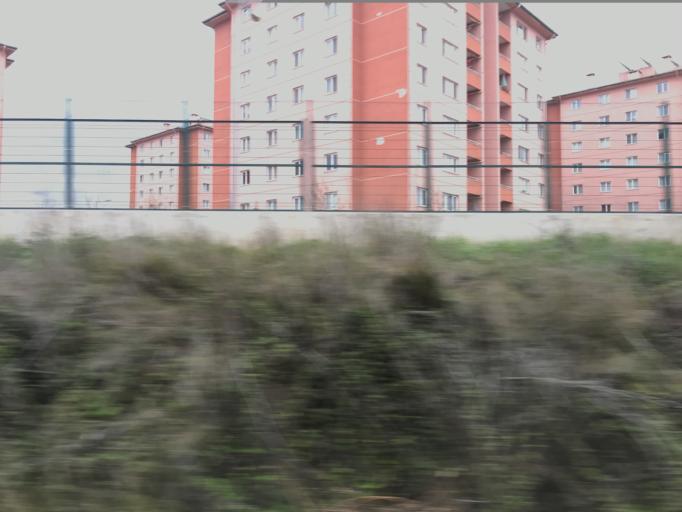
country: TR
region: Istanbul
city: Pendik
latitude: 40.8681
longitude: 29.2610
